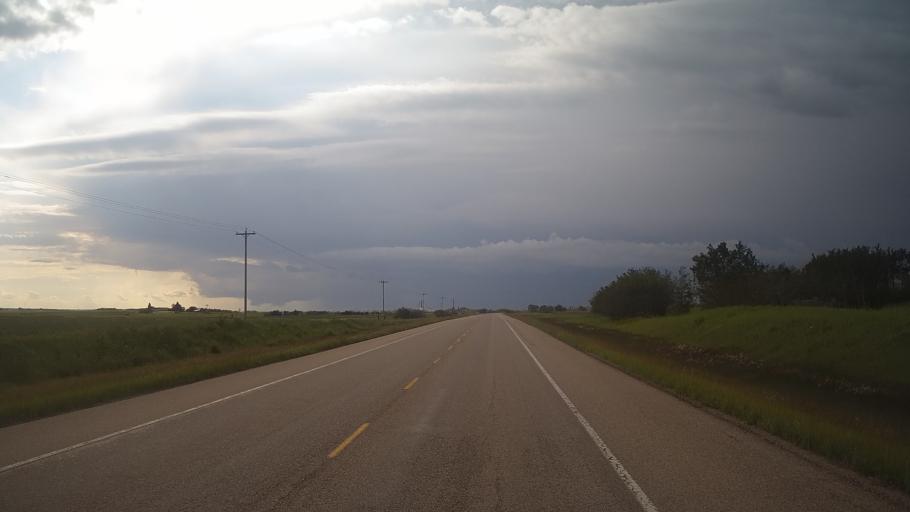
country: CA
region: Alberta
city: Vegreville
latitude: 53.2188
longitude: -112.1983
